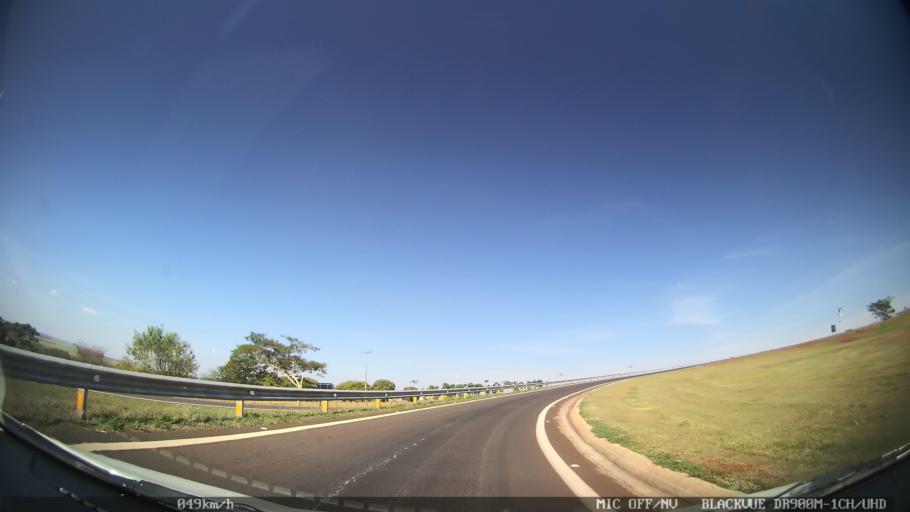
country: BR
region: Sao Paulo
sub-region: Jardinopolis
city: Jardinopolis
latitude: -21.0924
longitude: -47.7926
